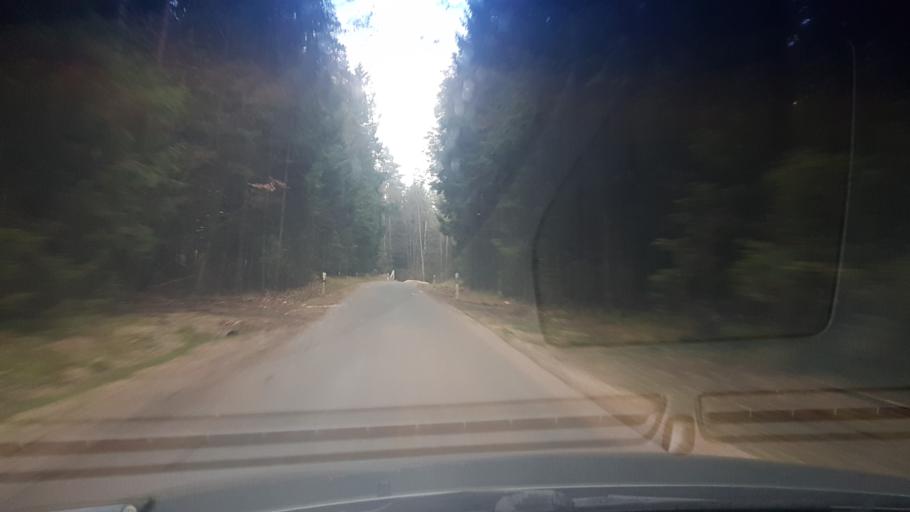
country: DE
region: Bavaria
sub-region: Upper Franconia
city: Weismain
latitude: 50.0505
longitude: 11.2873
